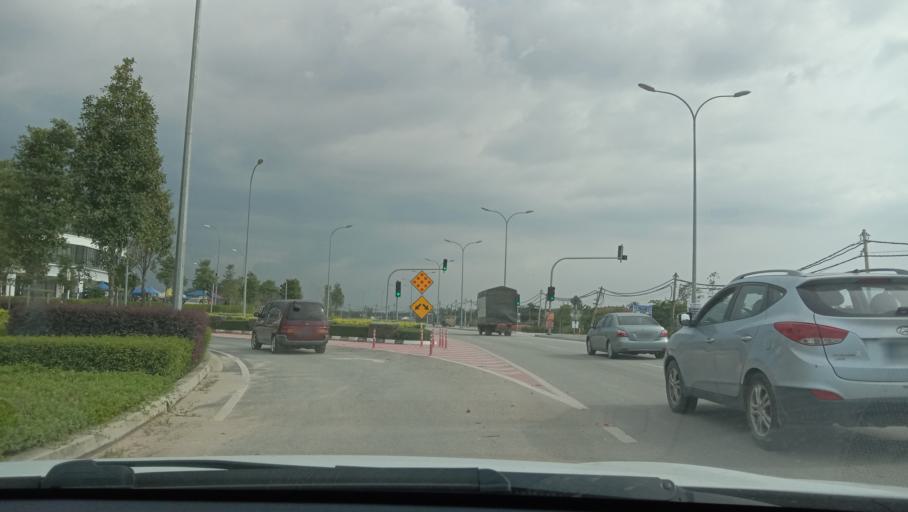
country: MY
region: Selangor
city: Ladang Seri Kundang
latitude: 3.2431
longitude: 101.4740
